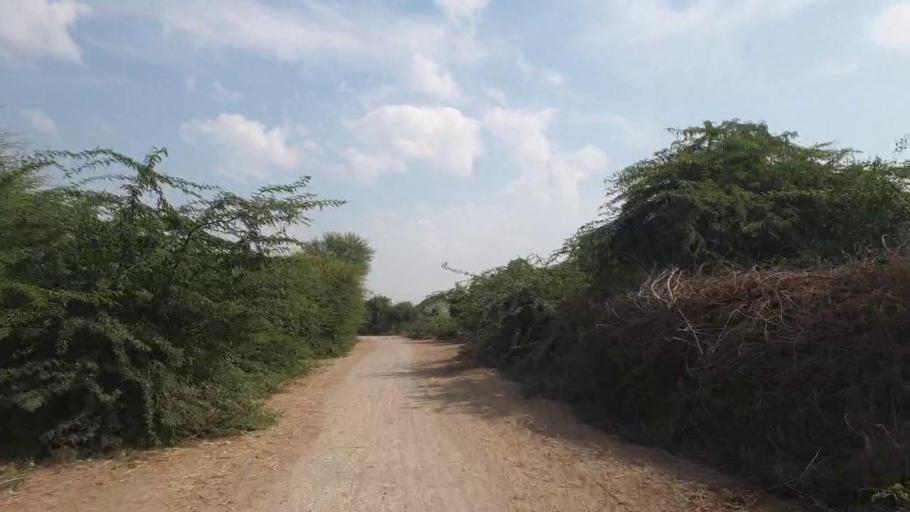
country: PK
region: Sindh
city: Rajo Khanani
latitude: 24.9371
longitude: 68.9958
